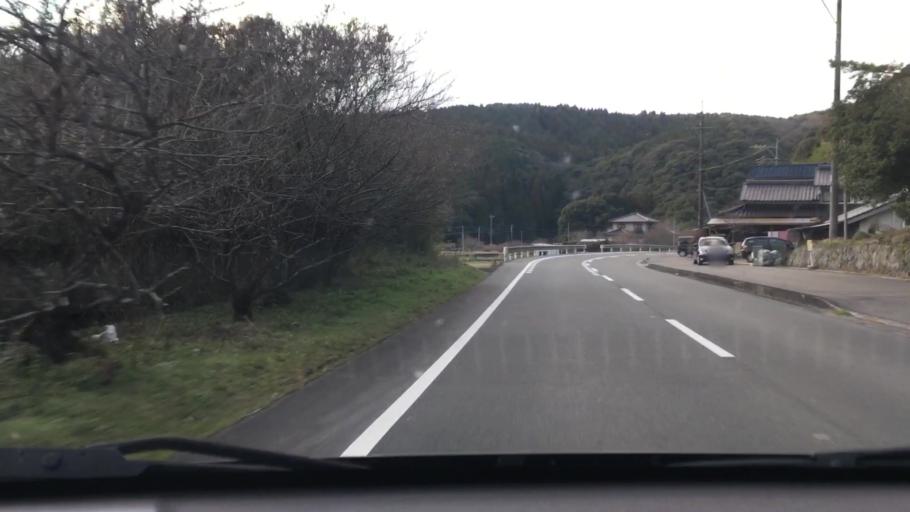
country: JP
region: Oita
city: Hiji
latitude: 33.4216
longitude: 131.4168
